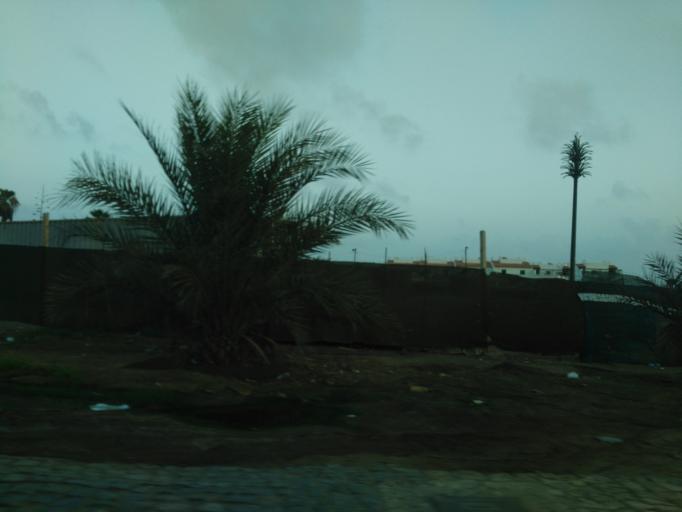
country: CV
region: Sal
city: Santa Maria
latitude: 16.6153
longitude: -22.9237
